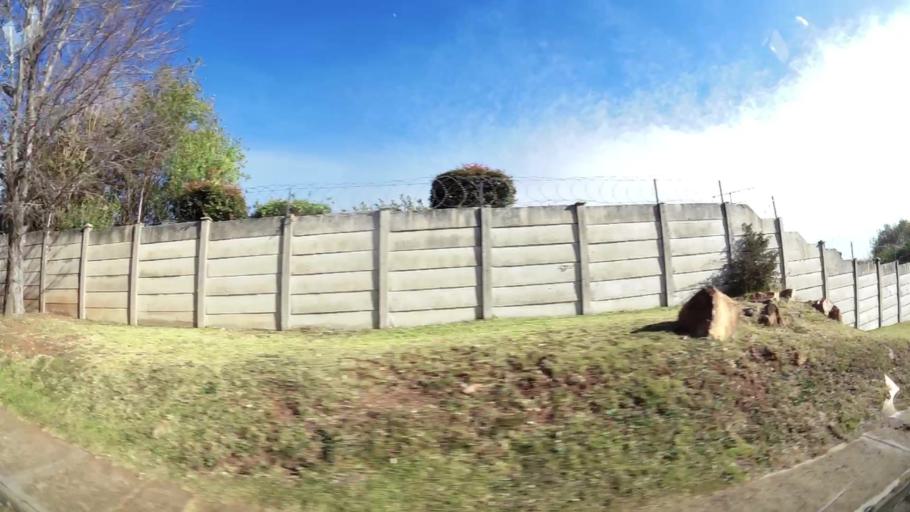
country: ZA
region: Gauteng
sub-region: City of Johannesburg Metropolitan Municipality
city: Roodepoort
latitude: -26.1227
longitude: 27.8490
